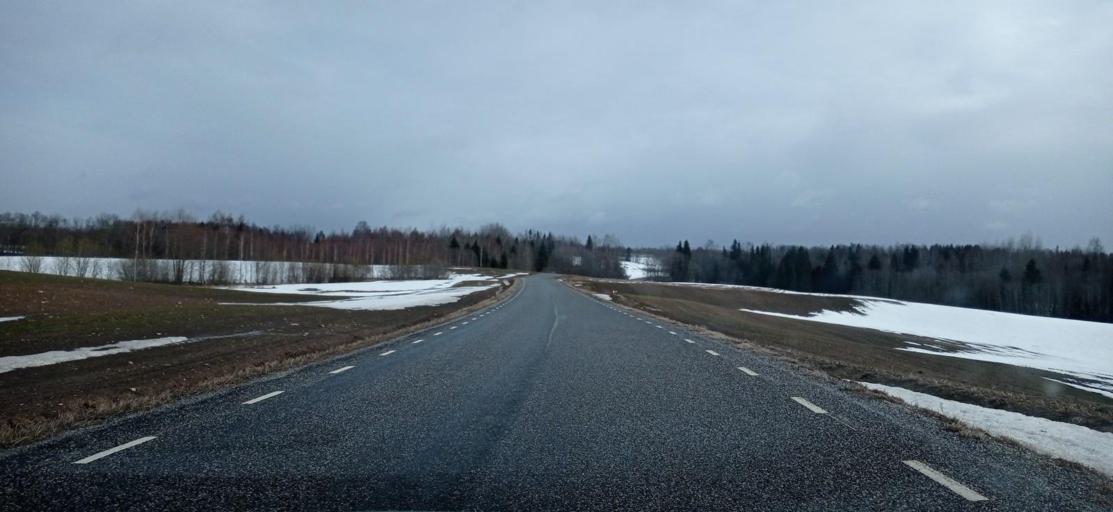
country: EE
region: Tartu
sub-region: Noo vald
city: Noo
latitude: 58.0824
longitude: 26.6695
